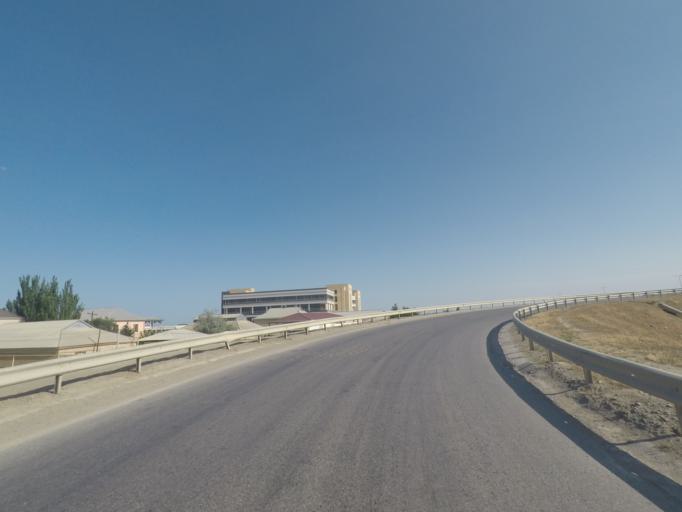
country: AZ
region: Baki
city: Qobustan
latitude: 40.0750
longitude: 49.4126
